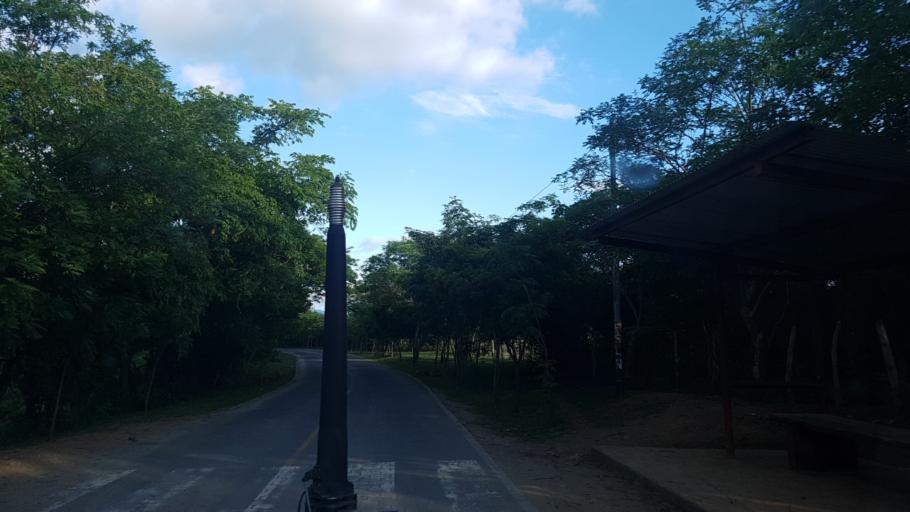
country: NI
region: Nueva Segovia
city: Ocotal
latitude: 13.6437
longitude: -86.6022
